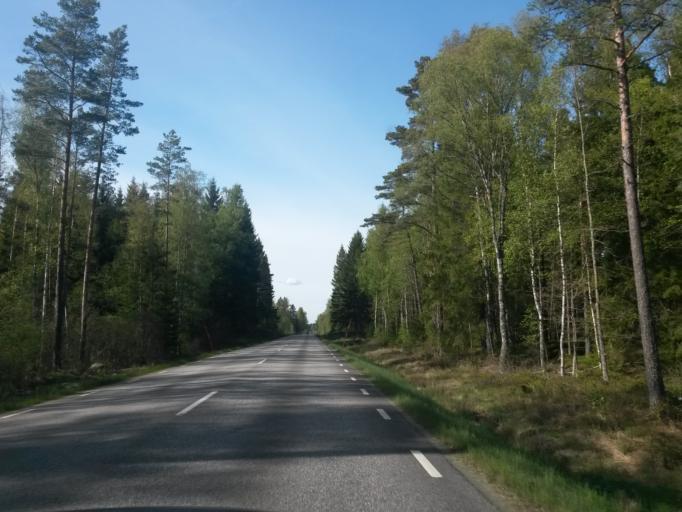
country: SE
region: Vaestra Goetaland
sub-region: Herrljunga Kommun
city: Herrljunga
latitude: 58.0376
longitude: 13.0463
